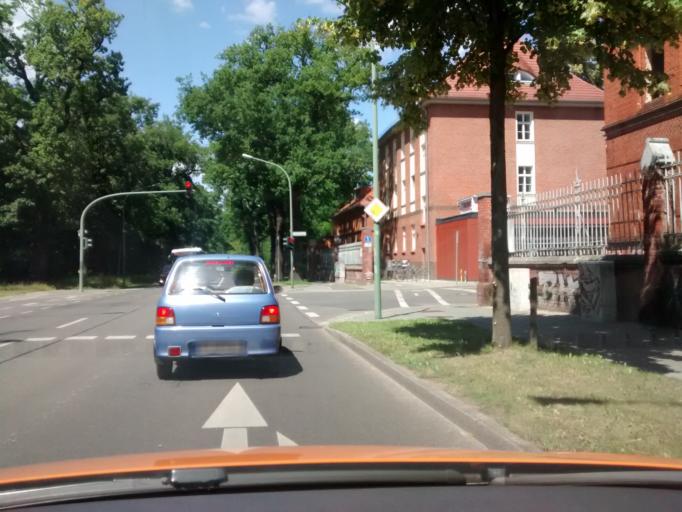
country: DE
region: Brandenburg
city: Potsdam
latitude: 52.4267
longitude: 13.0548
